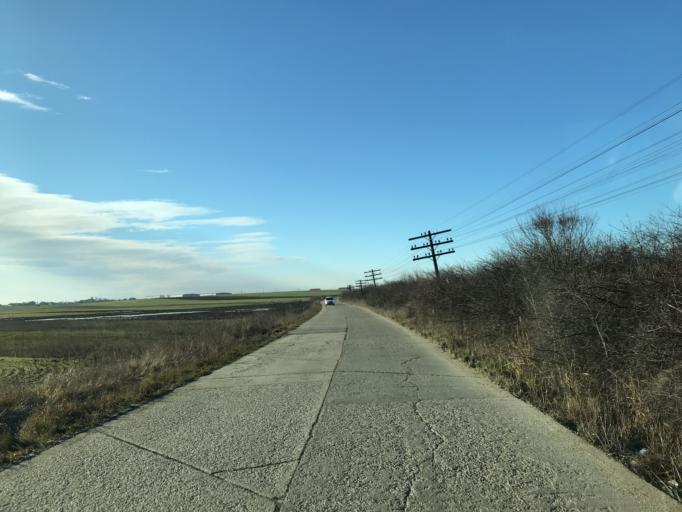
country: RO
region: Olt
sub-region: Comuna Piatra Olt
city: Piatra Olt
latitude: 44.3749
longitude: 24.2782
